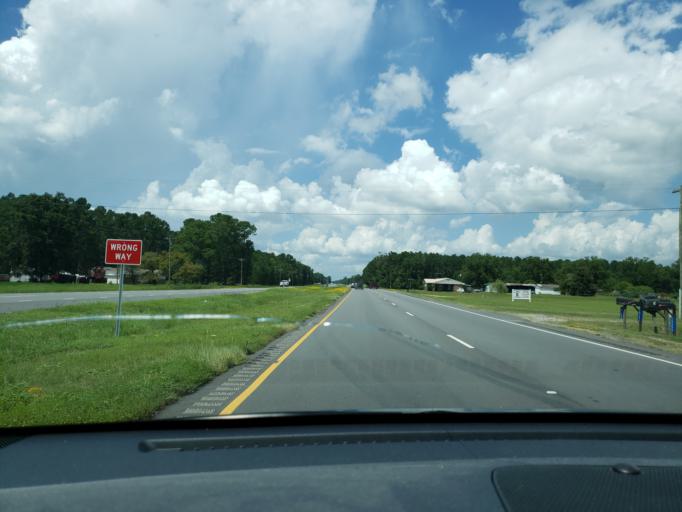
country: US
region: North Carolina
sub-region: Robeson County
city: Saint Pauls
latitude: 34.7951
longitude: -78.8190
